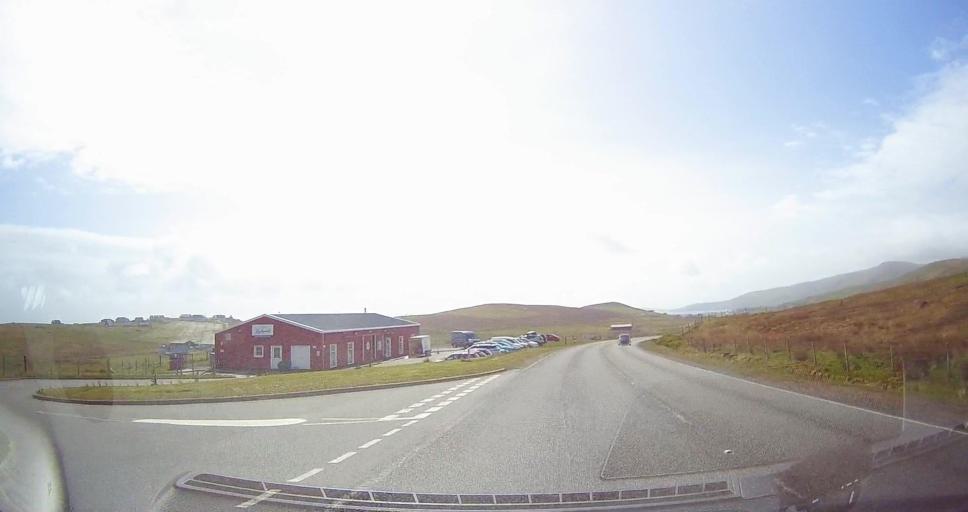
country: GB
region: Scotland
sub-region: Shetland Islands
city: Sandwick
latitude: 60.0647
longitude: -1.2224
